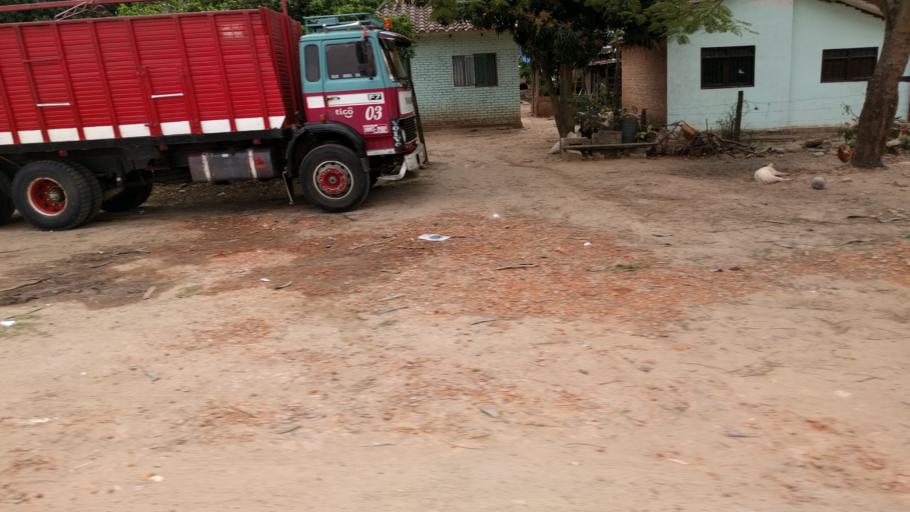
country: BO
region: Santa Cruz
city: Jorochito
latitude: -18.1338
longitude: -63.4725
